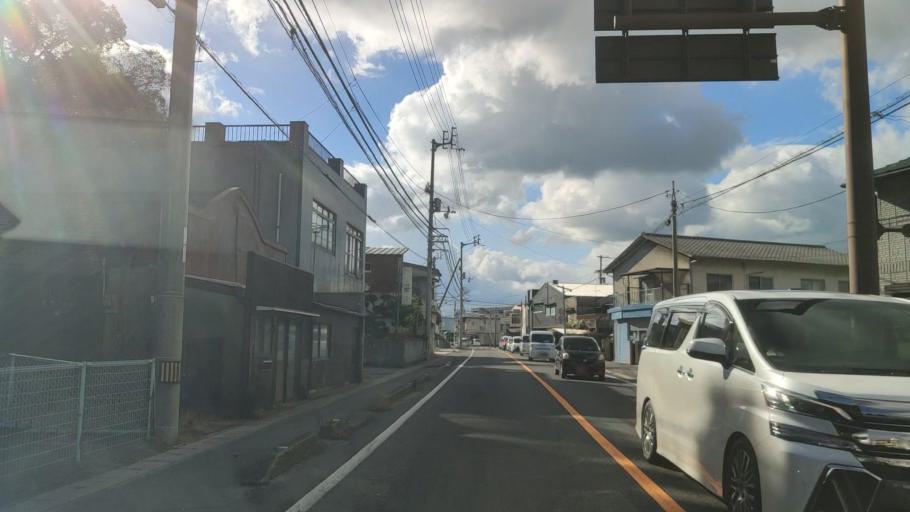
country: JP
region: Ehime
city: Masaki-cho
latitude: 33.8310
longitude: 132.7088
